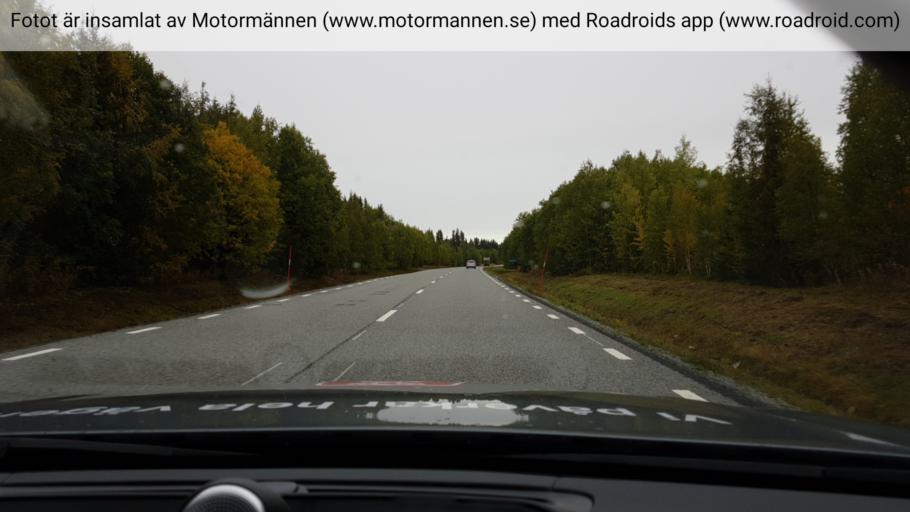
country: SE
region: Jaemtland
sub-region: Stroemsunds Kommun
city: Stroemsund
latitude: 64.0466
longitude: 15.5418
